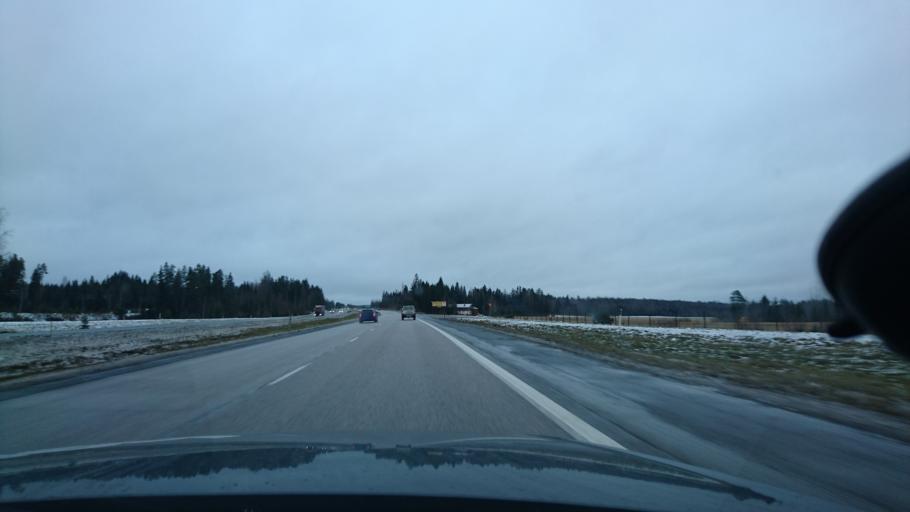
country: FI
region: Uusimaa
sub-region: Helsinki
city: Jaervenpaeae
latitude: 60.5493
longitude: 25.1841
